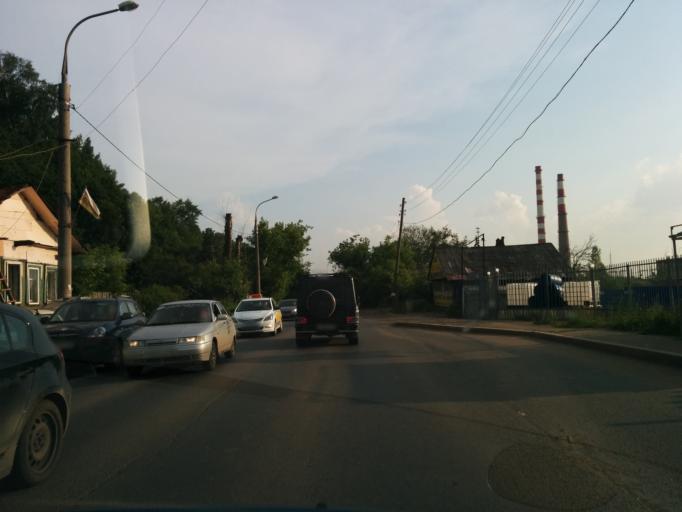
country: RU
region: Perm
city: Perm
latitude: 58.0481
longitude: 56.3240
